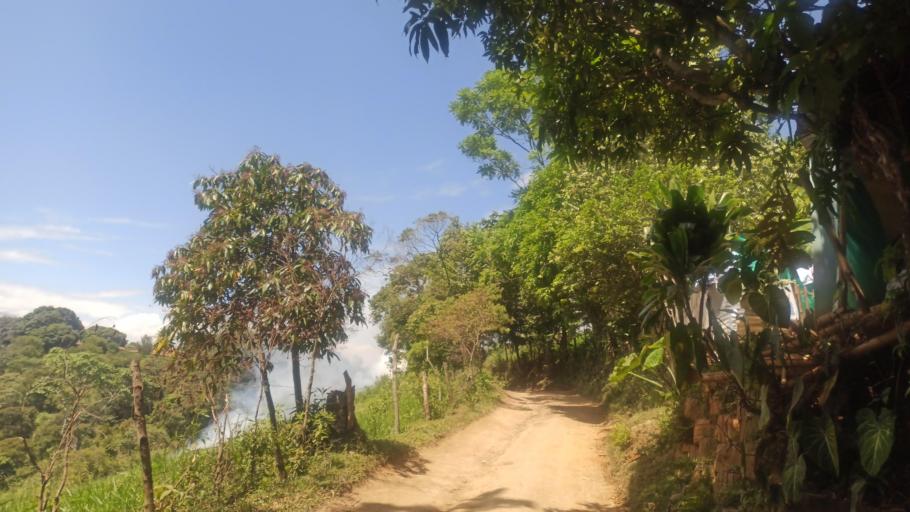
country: CO
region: Valle del Cauca
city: Jamundi
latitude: 3.1896
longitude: -76.6299
